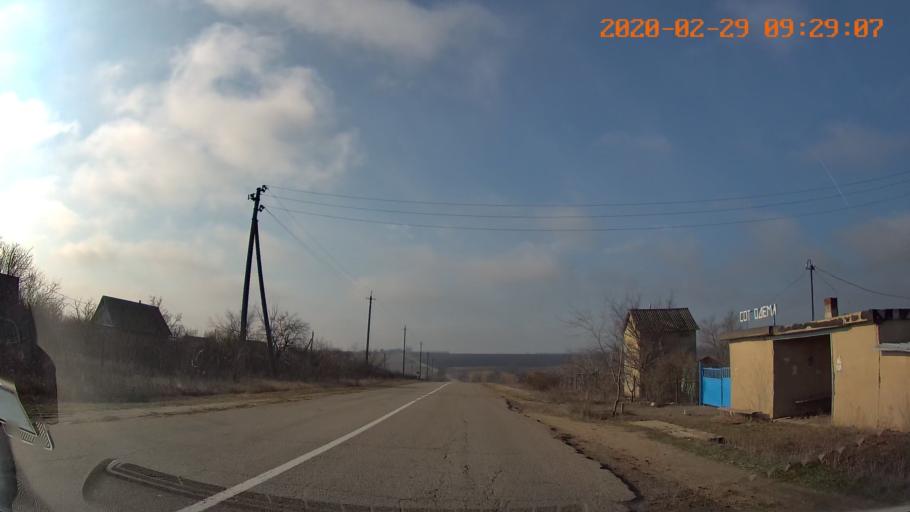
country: UA
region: Odessa
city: Lymanske
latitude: 46.6817
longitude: 29.9237
